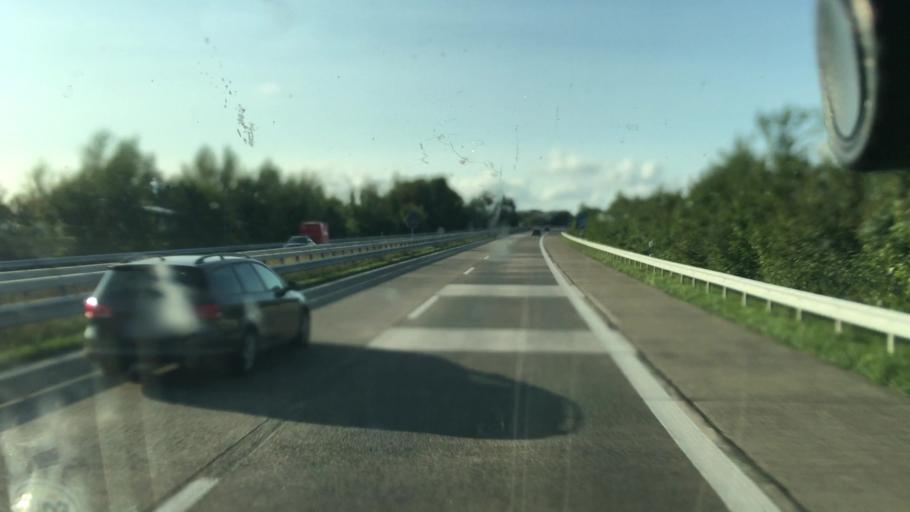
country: DE
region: Lower Saxony
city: Bockhorn
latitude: 53.4410
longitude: 8.0327
